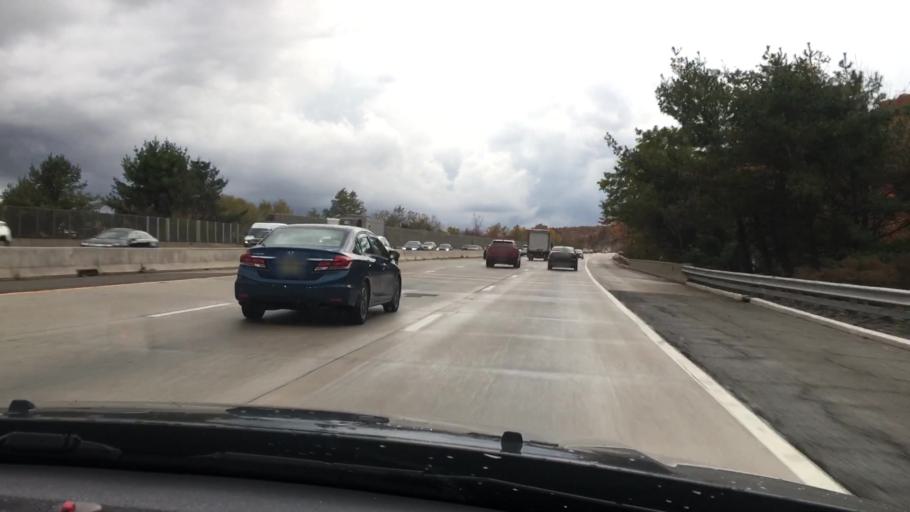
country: US
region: New Jersey
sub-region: Morris County
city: Riverdale
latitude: 40.9716
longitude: -74.3235
